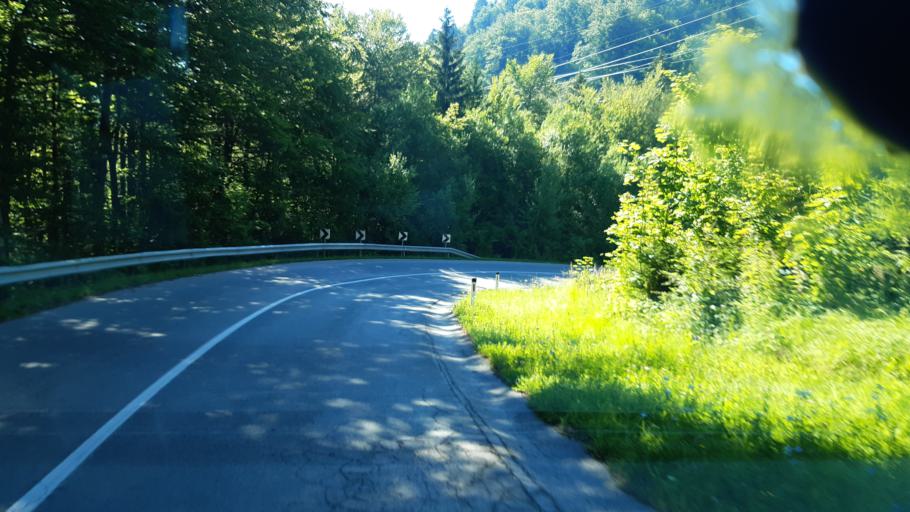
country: SI
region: Gornji Grad
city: Gornji Grad
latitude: 46.2148
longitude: 14.8069
